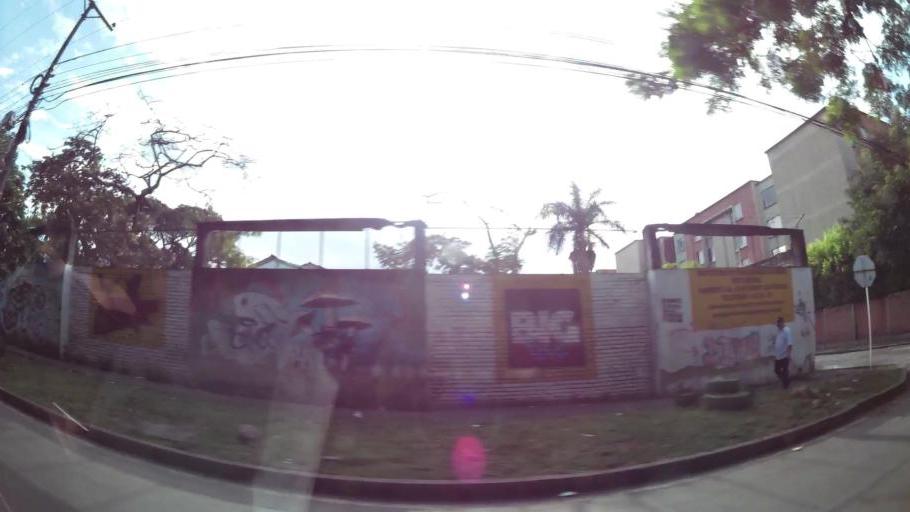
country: CO
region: Valle del Cauca
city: Cali
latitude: 3.4638
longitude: -76.5081
